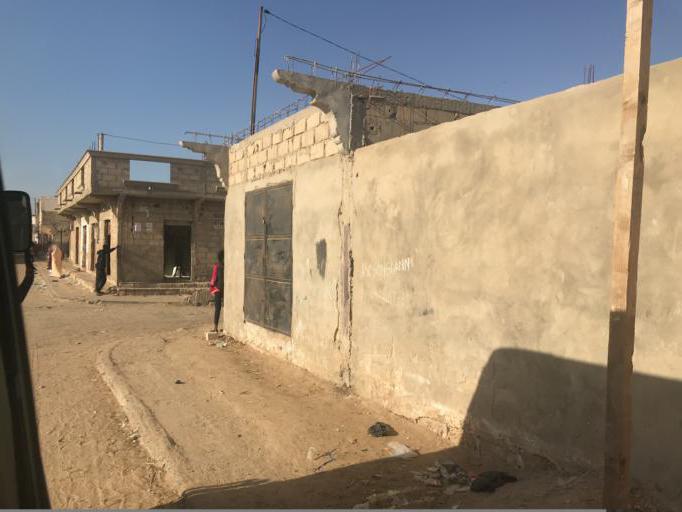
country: SN
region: Saint-Louis
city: Saint-Louis
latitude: 15.9977
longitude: -16.4948
